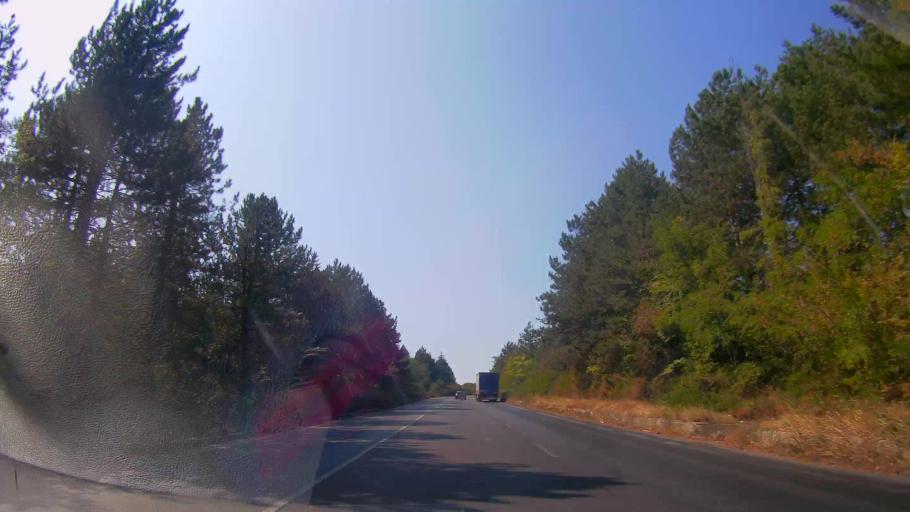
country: BG
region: Ruse
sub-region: Obshtina Vetovo
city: Senovo
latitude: 43.5609
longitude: 26.3755
